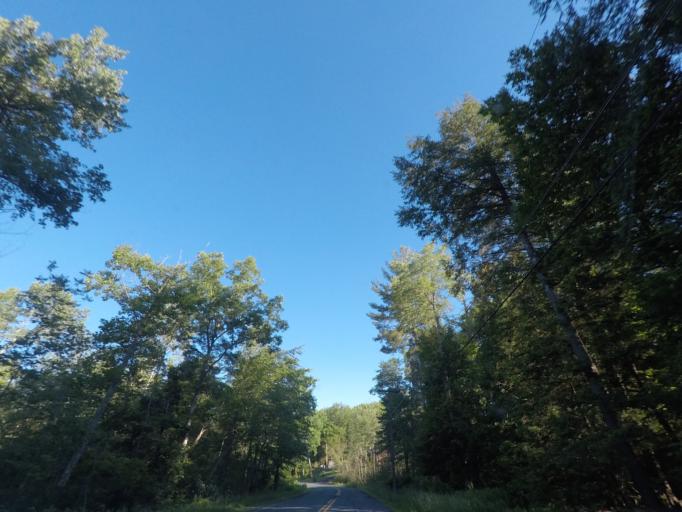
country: US
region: New York
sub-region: Rensselaer County
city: Averill Park
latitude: 42.5671
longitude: -73.5325
